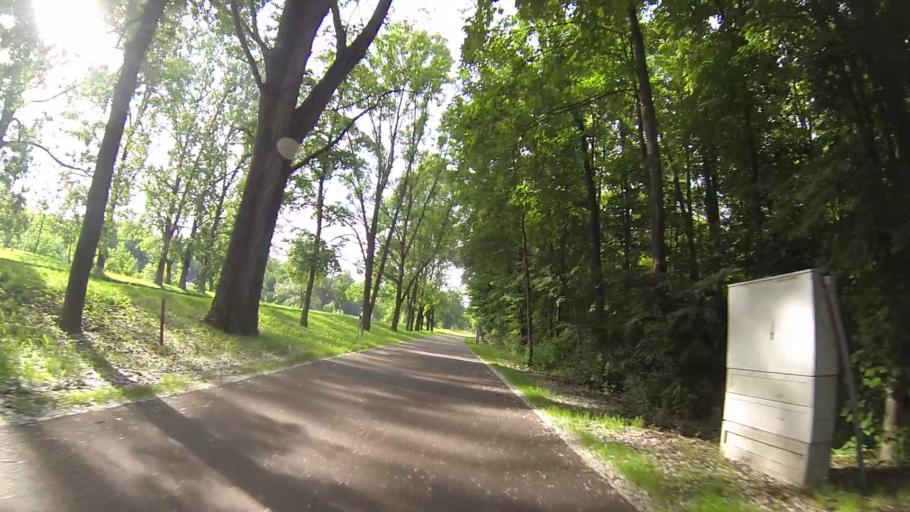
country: DE
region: Baden-Wuerttemberg
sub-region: Tuebingen Region
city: Ulm
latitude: 48.3652
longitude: 9.9664
